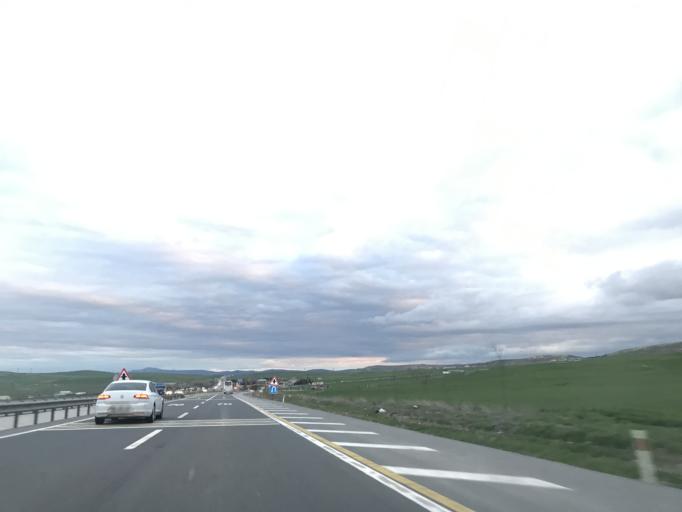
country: TR
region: Ankara
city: Ikizce
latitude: 39.5003
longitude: 32.8718
